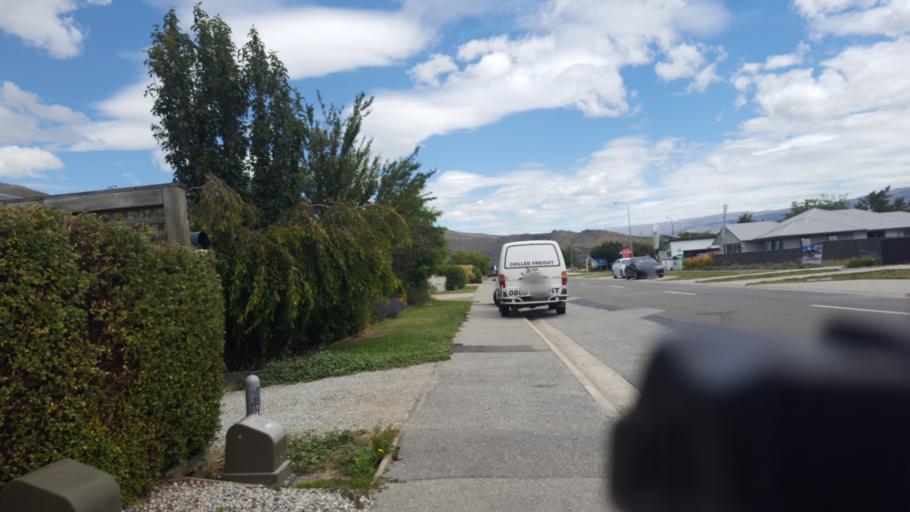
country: NZ
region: Otago
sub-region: Queenstown-Lakes District
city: Wanaka
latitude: -45.0380
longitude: 169.2160
